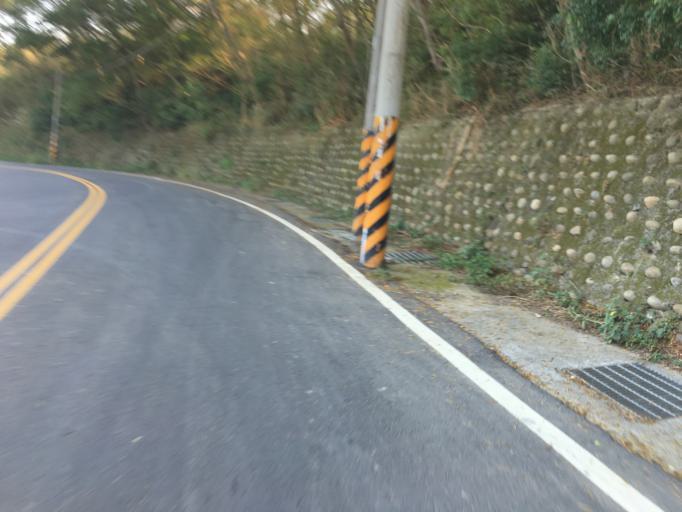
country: TW
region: Taiwan
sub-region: Hsinchu
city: Hsinchu
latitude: 24.7501
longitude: 121.0329
